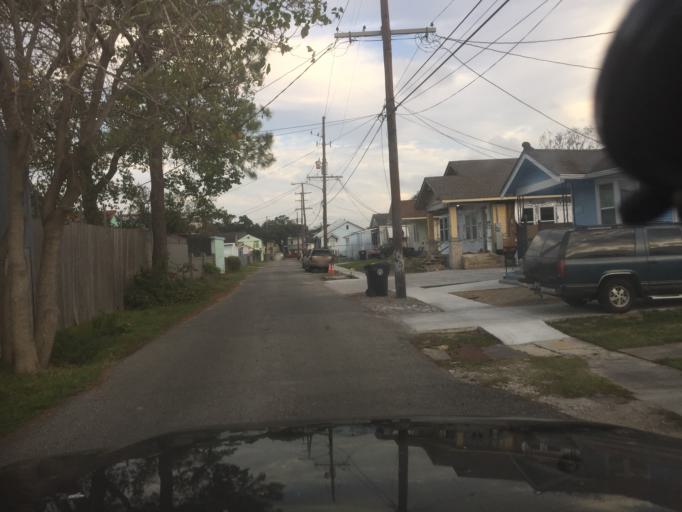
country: US
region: Louisiana
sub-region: Orleans Parish
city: New Orleans
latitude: 29.9866
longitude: -90.0780
